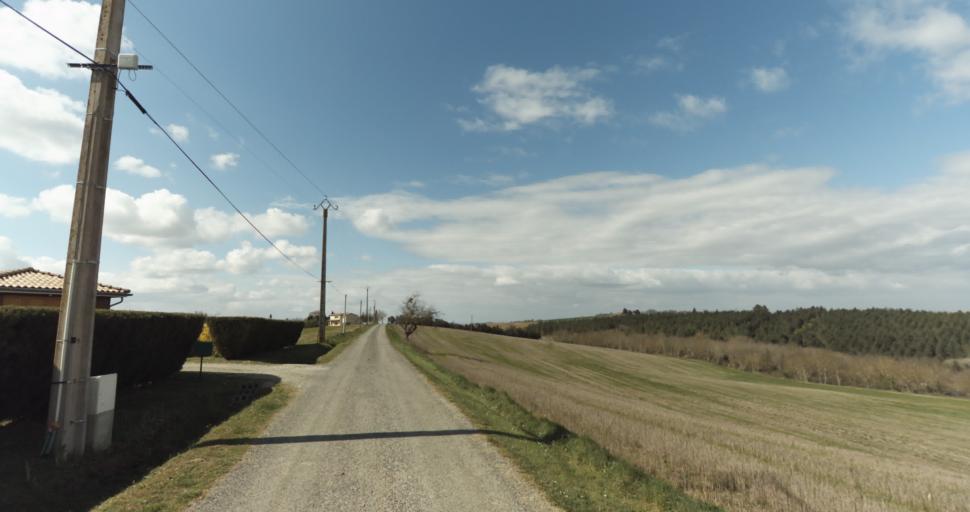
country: FR
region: Midi-Pyrenees
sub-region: Departement de la Haute-Garonne
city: Auterive
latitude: 43.3674
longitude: 1.5077
